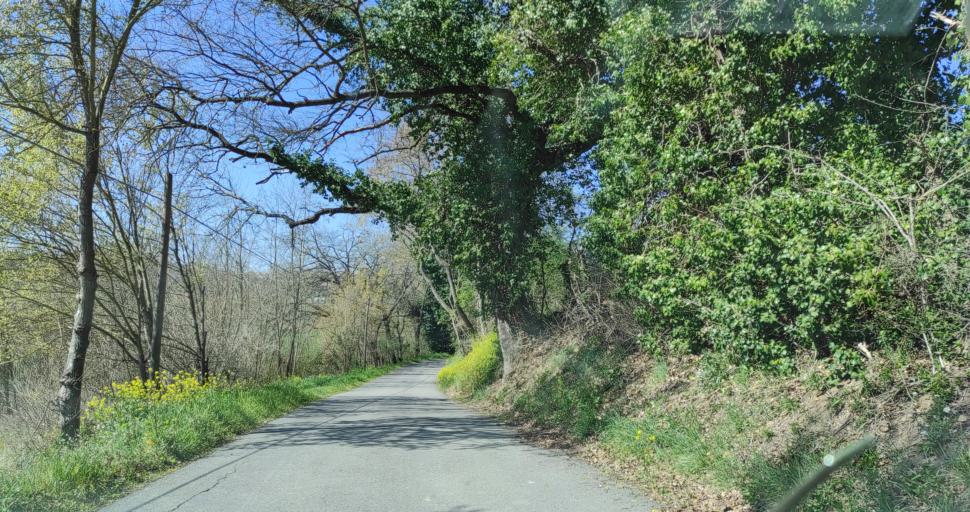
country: IT
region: The Marches
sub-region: Provincia di Macerata
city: Piediripa
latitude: 43.3123
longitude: 13.4881
